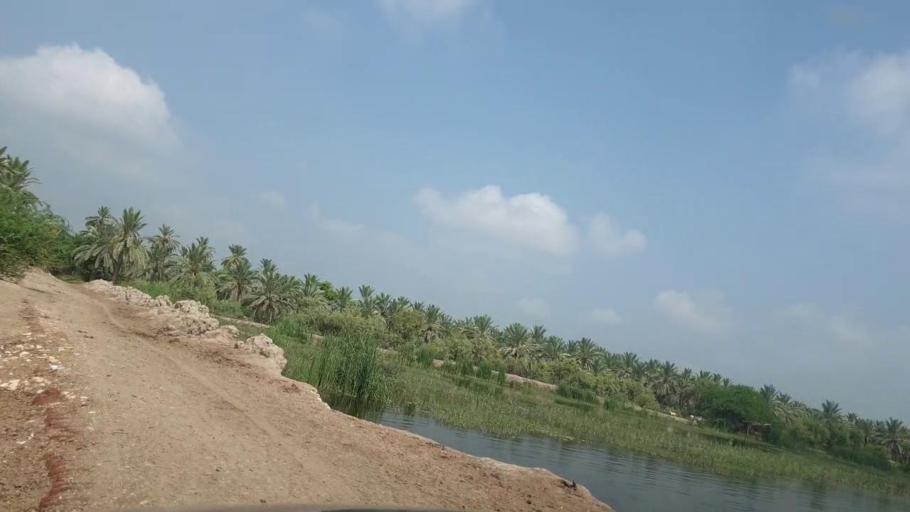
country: PK
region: Sindh
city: Pir jo Goth
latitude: 27.6040
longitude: 68.7024
